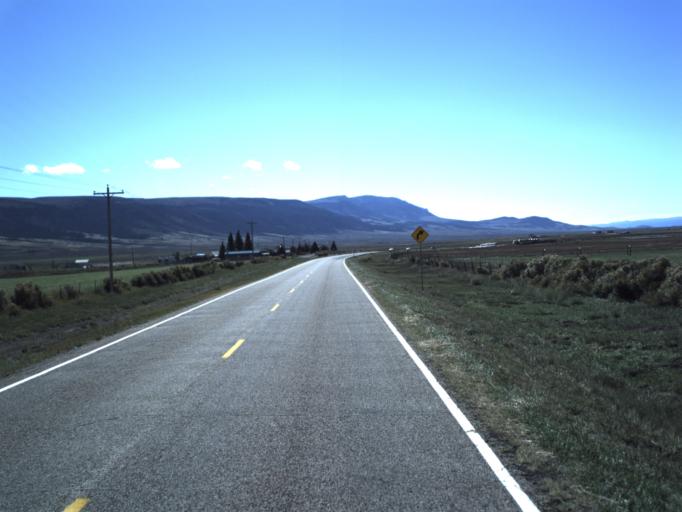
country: US
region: Utah
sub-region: Wayne County
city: Loa
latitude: 38.4982
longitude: -111.8813
